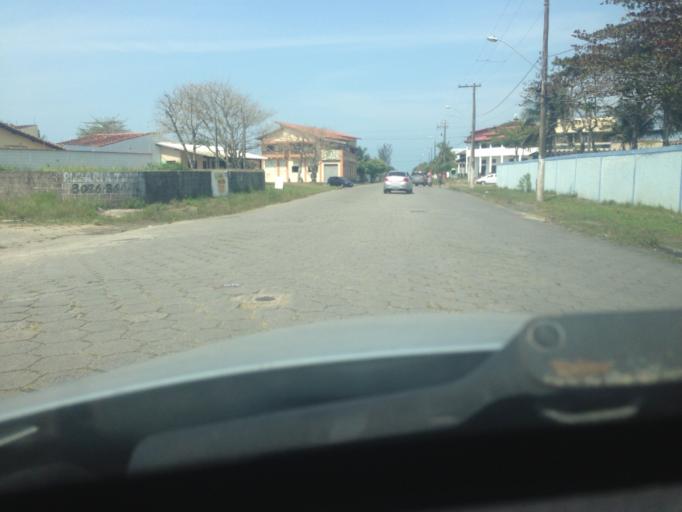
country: BR
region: Sao Paulo
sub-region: Itanhaem
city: Itanhaem
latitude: -24.2221
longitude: -46.8627
